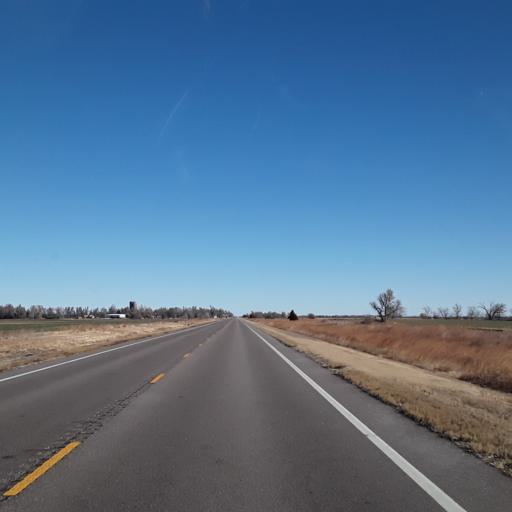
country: US
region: Kansas
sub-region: Pawnee County
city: Larned
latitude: 38.1108
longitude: -99.1925
